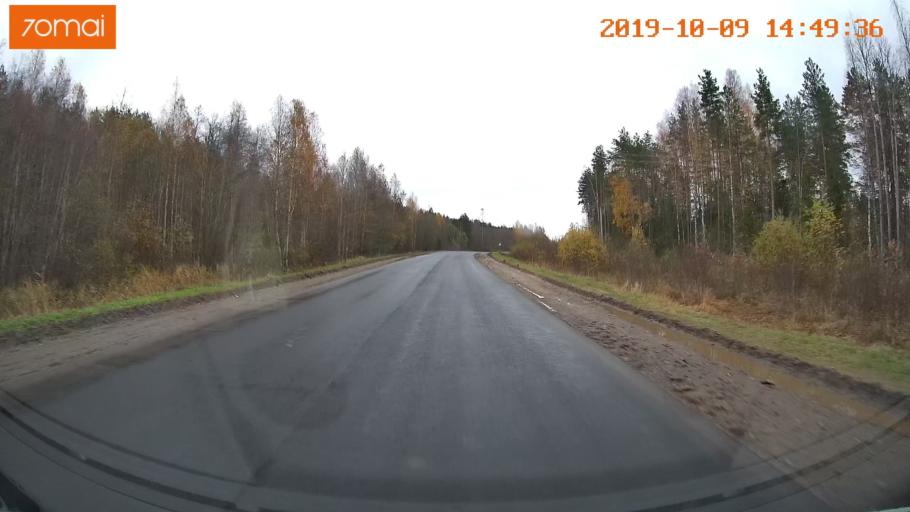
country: RU
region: Kostroma
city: Chistyye Bory
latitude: 58.3917
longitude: 41.5845
